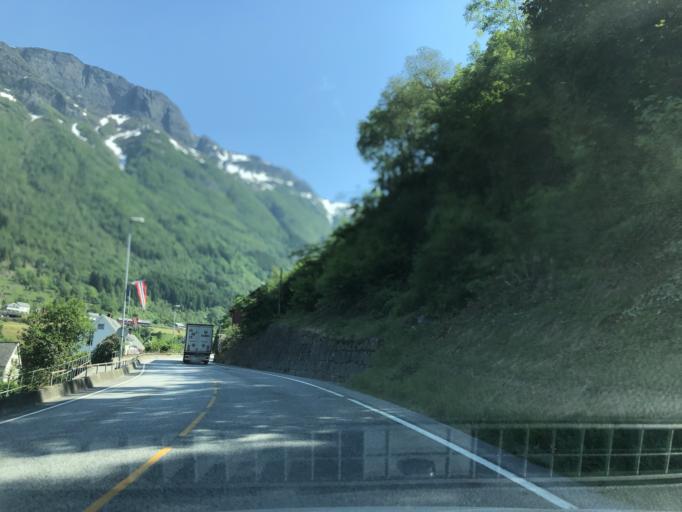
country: NO
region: Hordaland
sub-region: Odda
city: Odda
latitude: 60.0579
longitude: 6.5477
